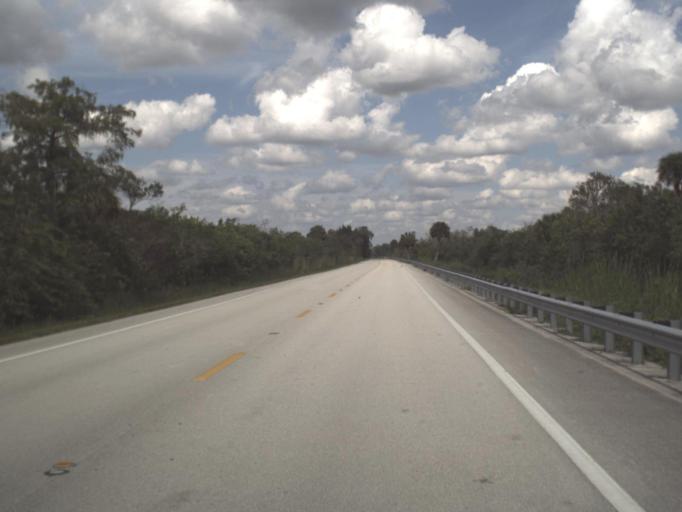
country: US
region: Florida
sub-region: Collier County
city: Lely Resort
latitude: 25.9274
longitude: -81.3577
